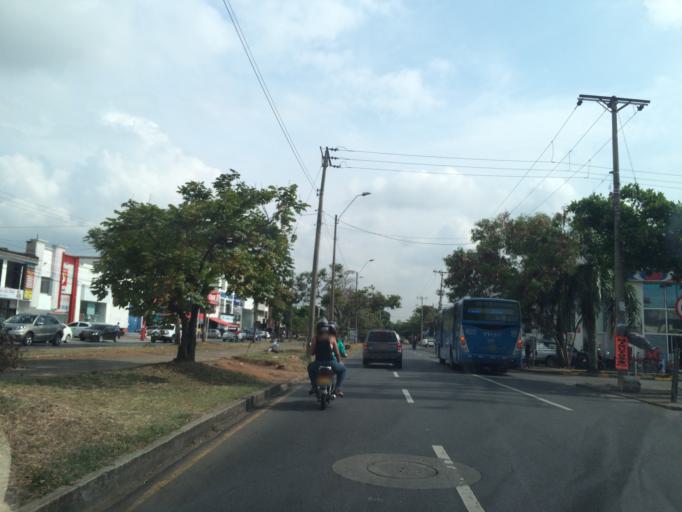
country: CO
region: Valle del Cauca
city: Cali
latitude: 3.3883
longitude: -76.5386
